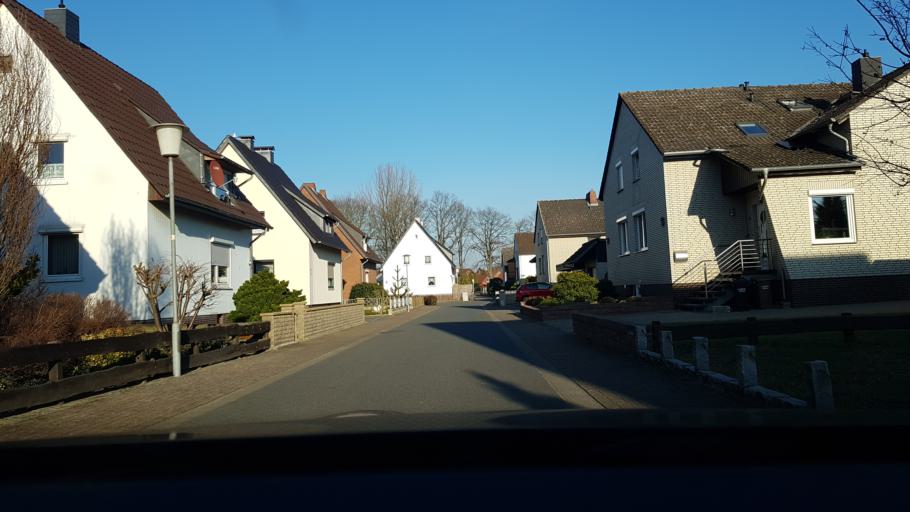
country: DE
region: Lower Saxony
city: Gifhorn
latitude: 52.5058
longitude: 10.5768
